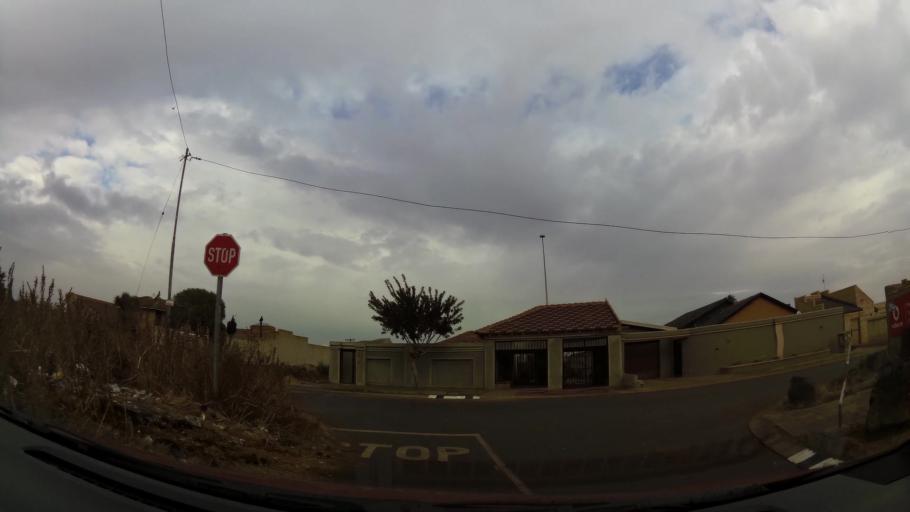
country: ZA
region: Gauteng
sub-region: City of Johannesburg Metropolitan Municipality
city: Soweto
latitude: -26.2825
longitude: 27.8371
